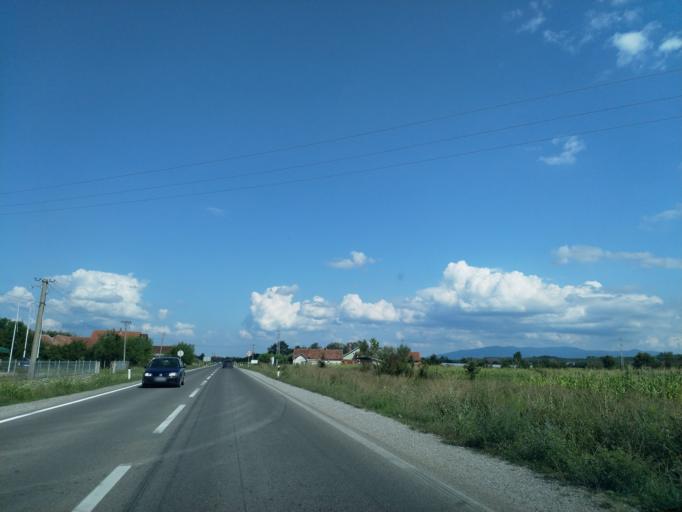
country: RS
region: Central Serbia
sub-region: Rasinski Okrug
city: Trstenik
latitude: 43.5789
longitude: 21.1345
